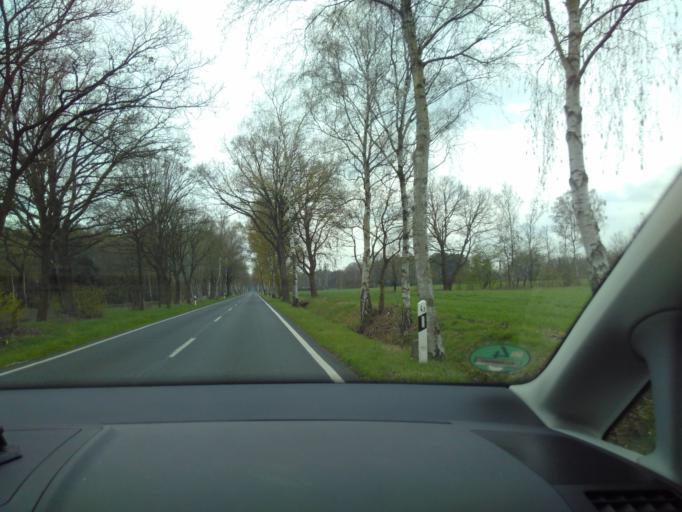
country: DE
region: Lower Saxony
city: Adelheidsdorf
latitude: 52.5796
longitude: 10.0228
